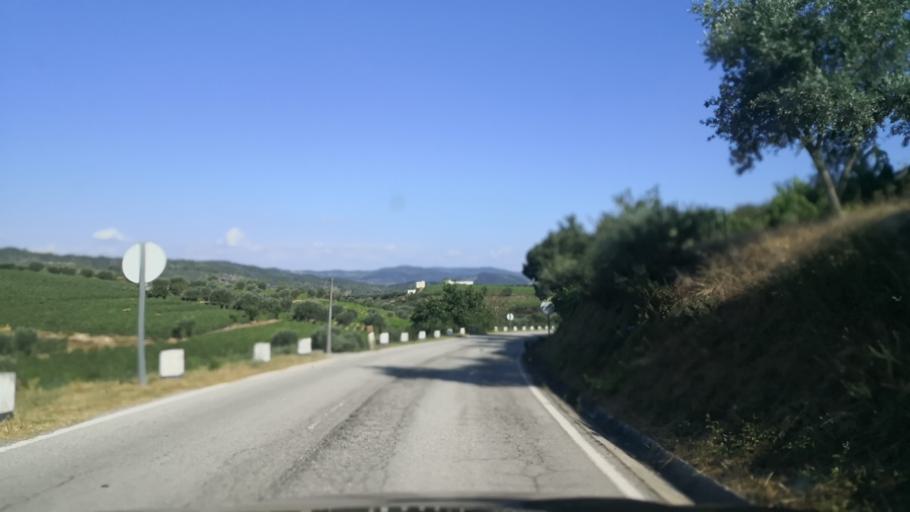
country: PT
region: Vila Real
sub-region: Sabrosa
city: Sabrosa
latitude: 41.2755
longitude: -7.4618
